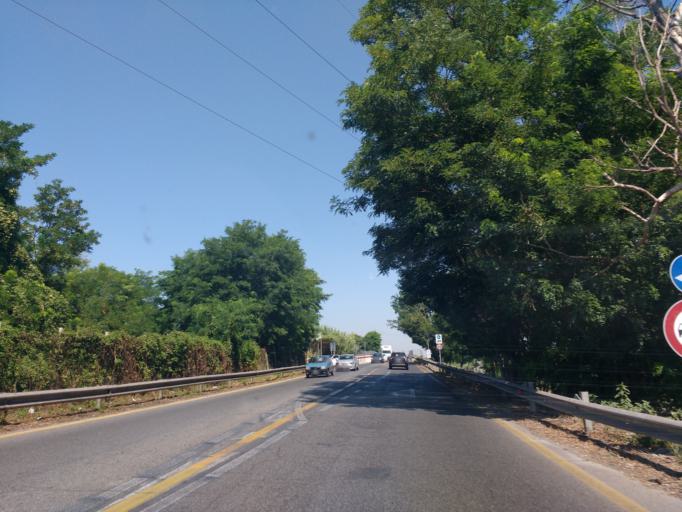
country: IT
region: Latium
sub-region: Citta metropolitana di Roma Capitale
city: Lido di Ostia
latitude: 41.7527
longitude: 12.2793
